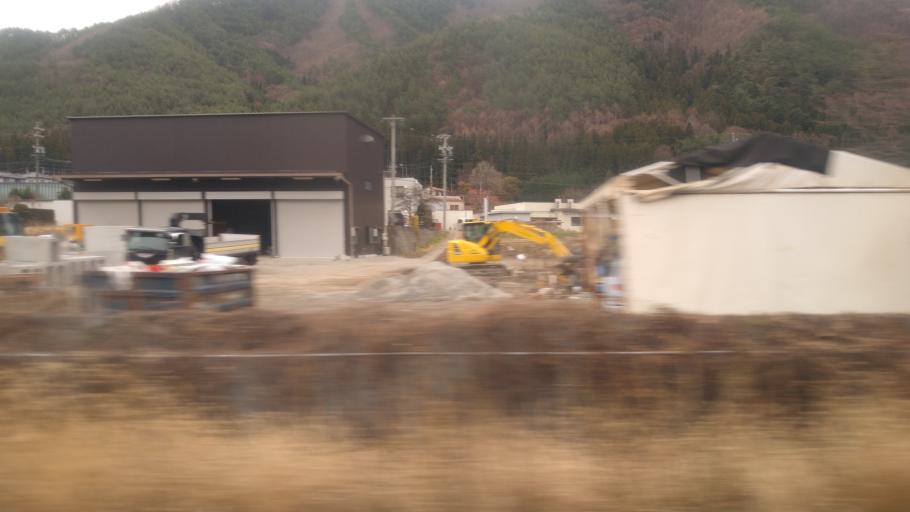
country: JP
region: Nagano
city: Shiojiri
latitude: 36.0675
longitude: 137.9018
